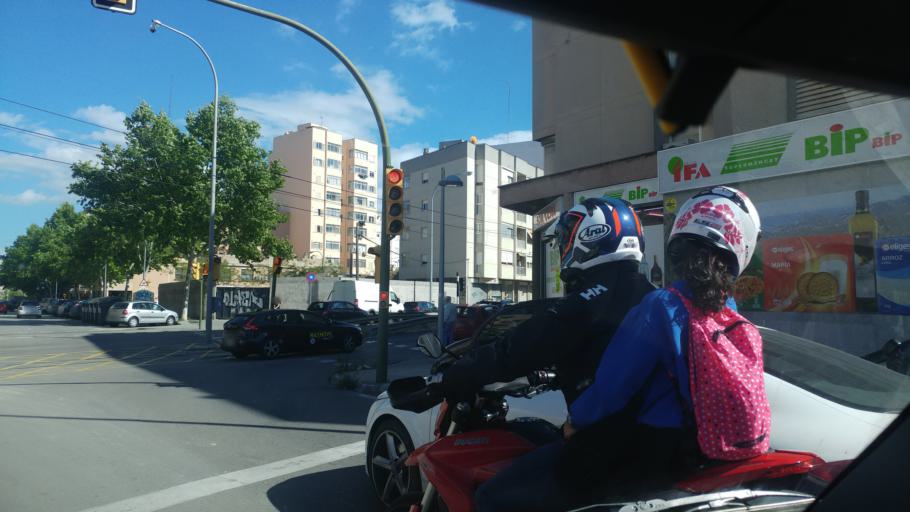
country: ES
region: Balearic Islands
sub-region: Illes Balears
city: Palma
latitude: 39.5879
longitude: 2.6607
